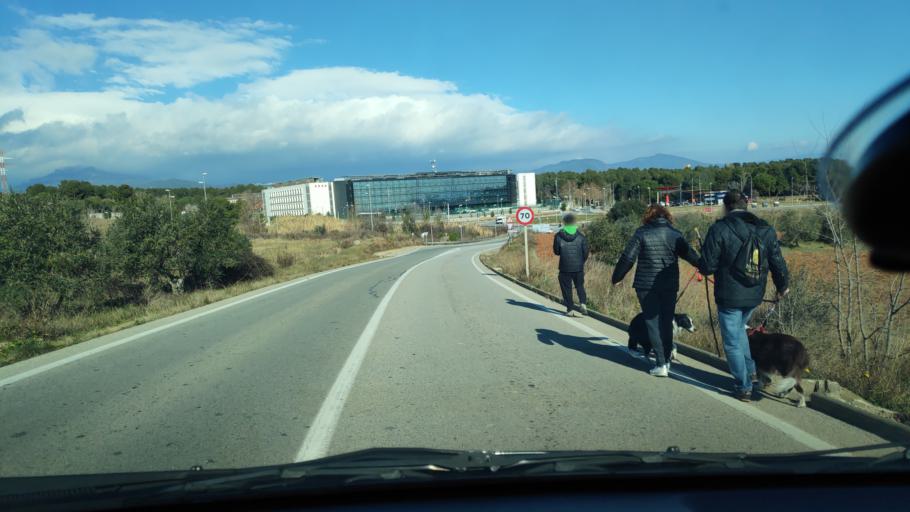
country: ES
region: Catalonia
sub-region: Provincia de Barcelona
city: Sant Quirze del Valles
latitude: 41.5507
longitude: 2.0673
